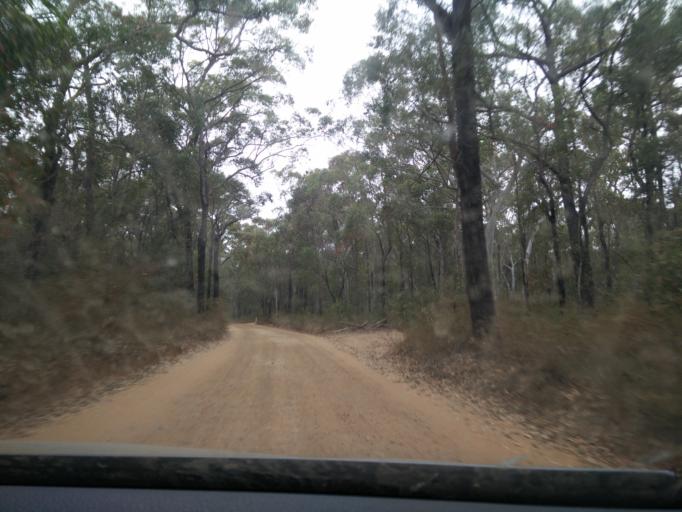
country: AU
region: New South Wales
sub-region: Blue Mountains Municipality
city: Glenbrook
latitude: -33.8001
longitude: 150.5933
